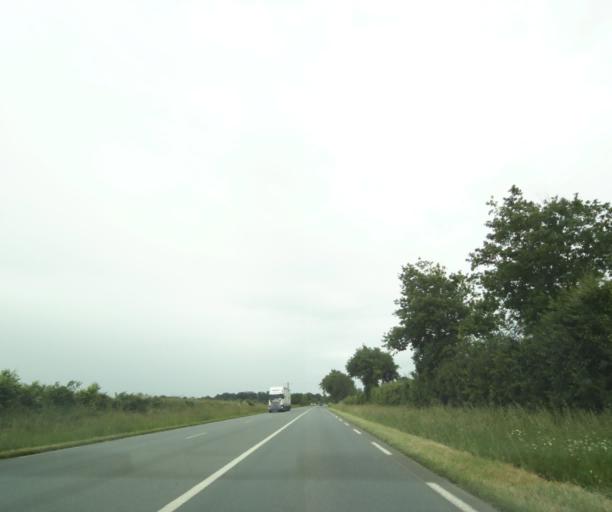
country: FR
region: Poitou-Charentes
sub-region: Departement des Deux-Sevres
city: Champdeniers-Saint-Denis
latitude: 46.4608
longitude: -0.3756
